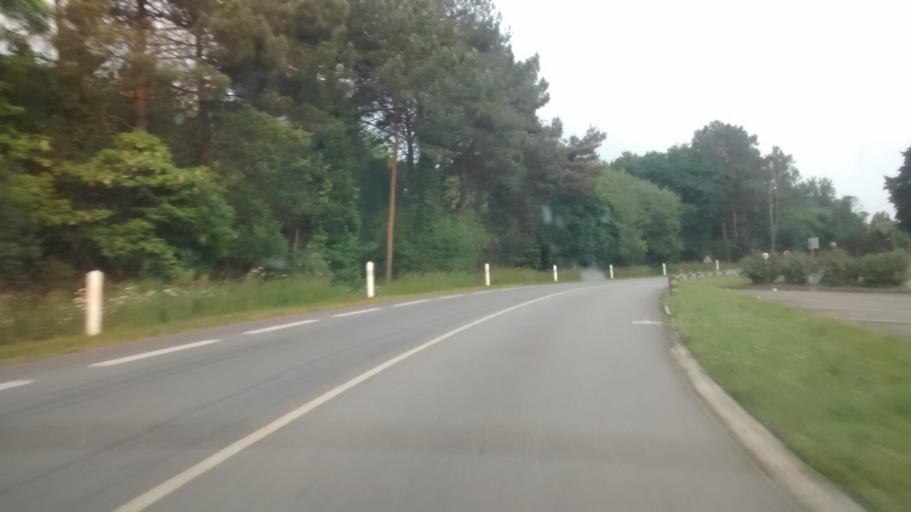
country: FR
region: Brittany
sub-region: Departement du Morbihan
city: Beignon
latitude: 47.9517
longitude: -2.1357
